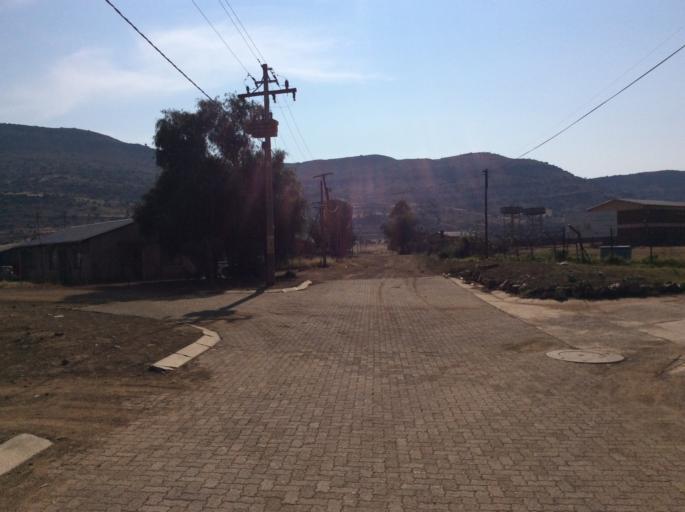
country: LS
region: Mafeteng
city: Mafeteng
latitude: -29.7171
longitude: 27.0299
